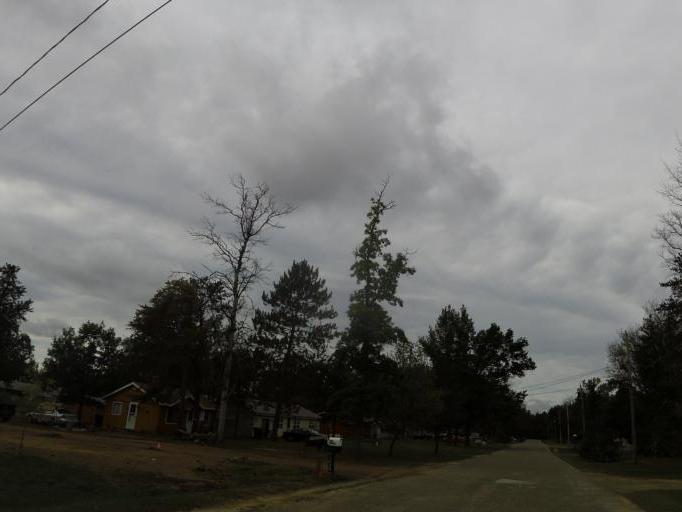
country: US
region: Michigan
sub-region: Roscommon County
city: Saint Helen
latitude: 44.3493
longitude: -84.4326
